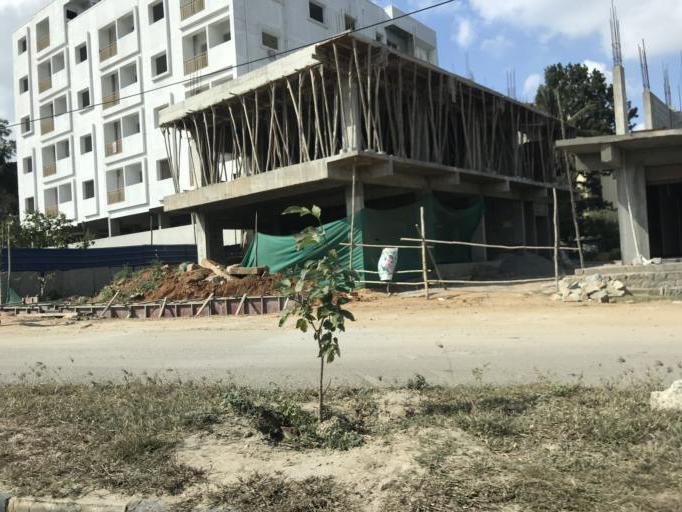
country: IN
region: Karnataka
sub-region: Bangalore Urban
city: Bangalore
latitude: 12.8526
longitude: 77.5871
